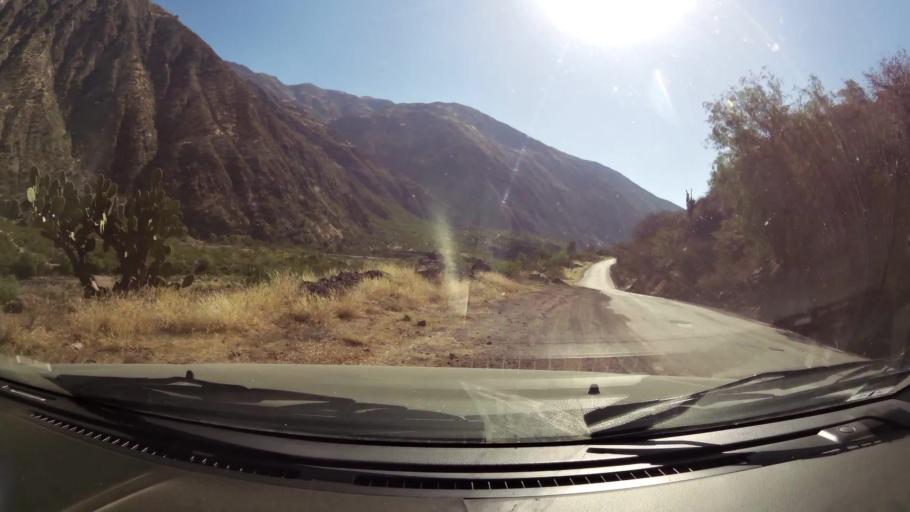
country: PE
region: Huancavelica
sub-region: Provincia de Acobamba
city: Pomacocha
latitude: -12.7565
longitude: -74.5268
